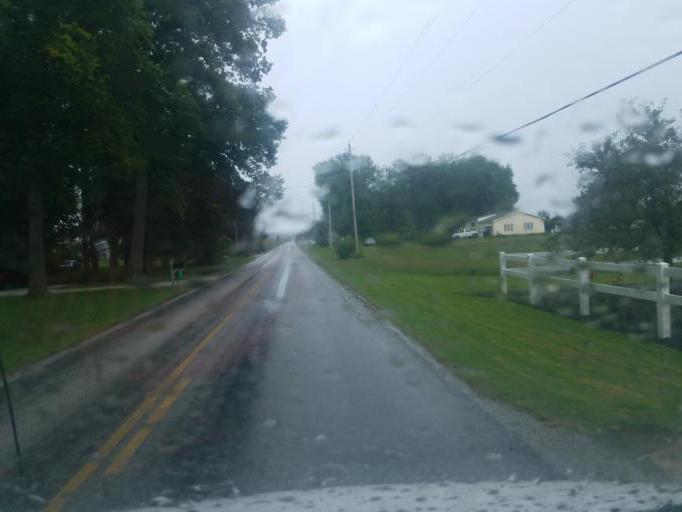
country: US
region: Ohio
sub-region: Wayne County
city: Creston
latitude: 40.9823
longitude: -81.8756
